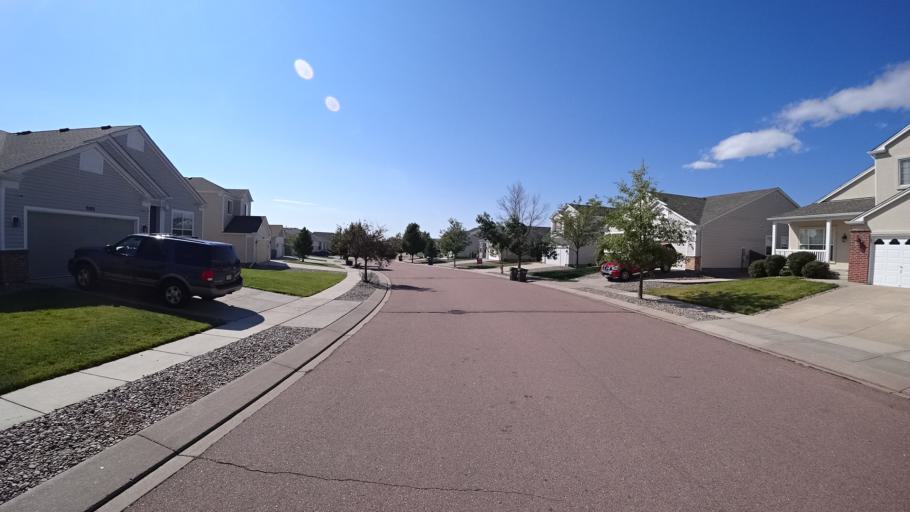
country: US
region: Colorado
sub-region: El Paso County
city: Cimarron Hills
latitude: 38.9284
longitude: -104.6958
